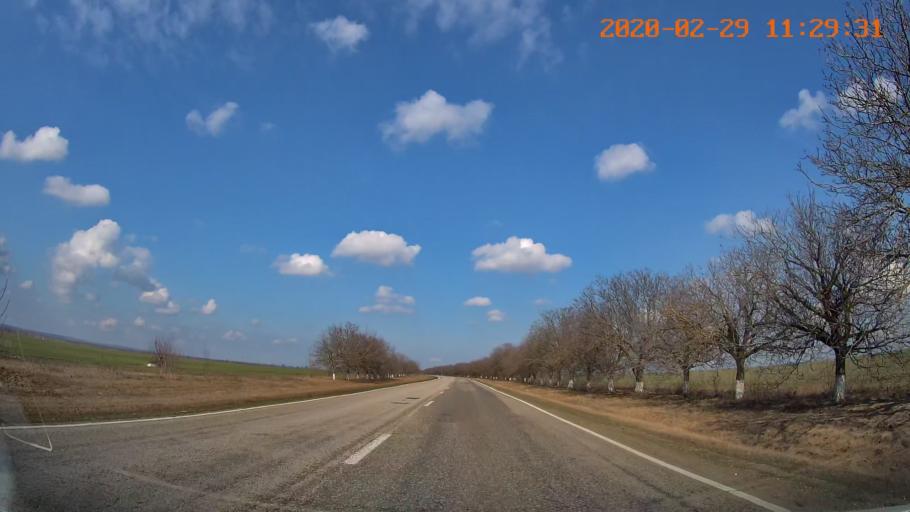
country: MD
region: Telenesti
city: Cocieri
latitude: 47.4957
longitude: 29.1249
